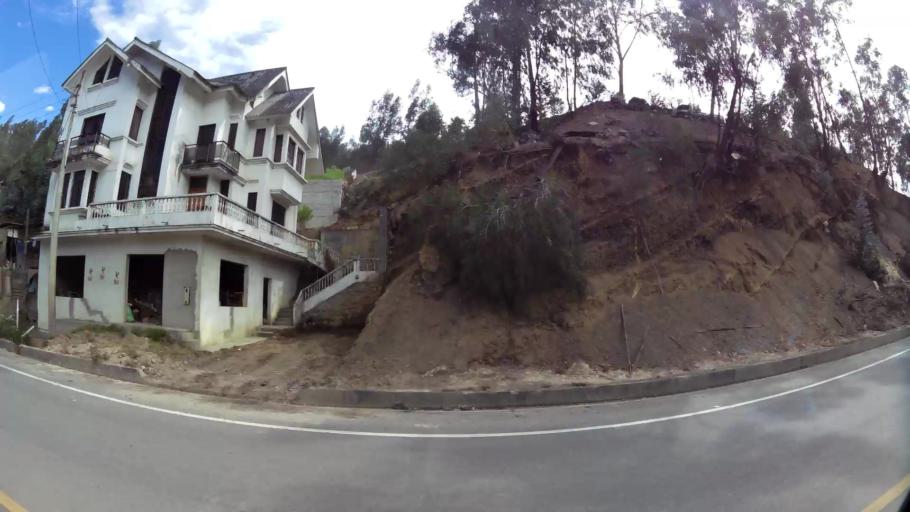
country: EC
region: Canar
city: Azogues
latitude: -2.7246
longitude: -78.8714
